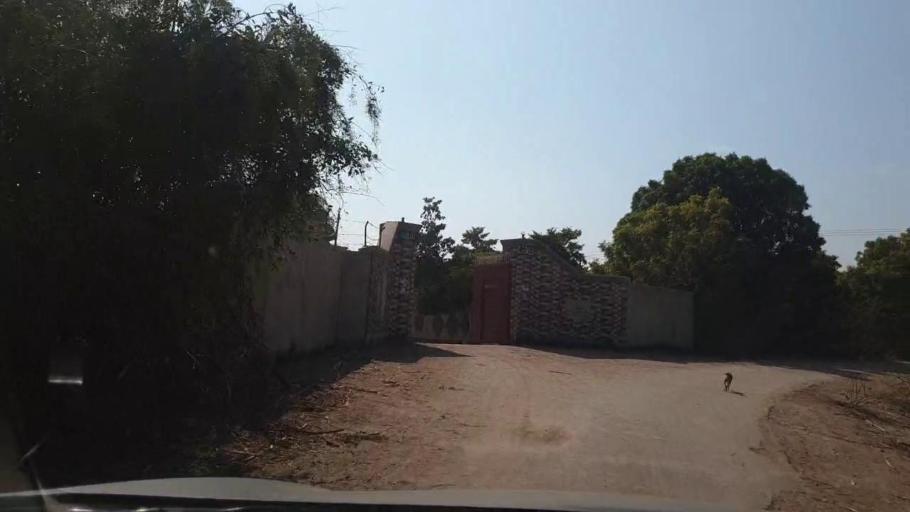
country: PK
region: Sindh
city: Tando Allahyar
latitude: 25.4719
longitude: 68.6509
